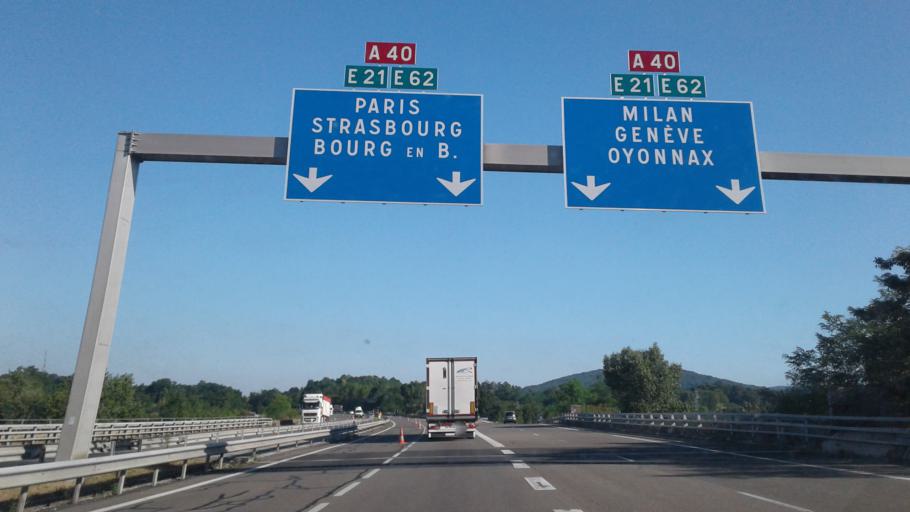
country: FR
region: Rhone-Alpes
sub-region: Departement de l'Ain
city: Saint-Martin-du-Mont
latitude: 46.0635
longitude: 5.3286
